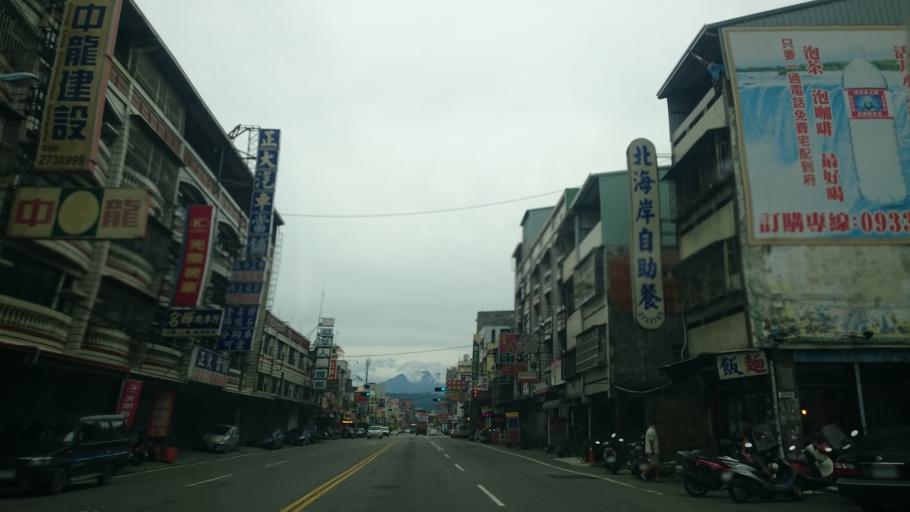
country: TW
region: Taiwan
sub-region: Nantou
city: Nantou
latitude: 23.8402
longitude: 120.7013
